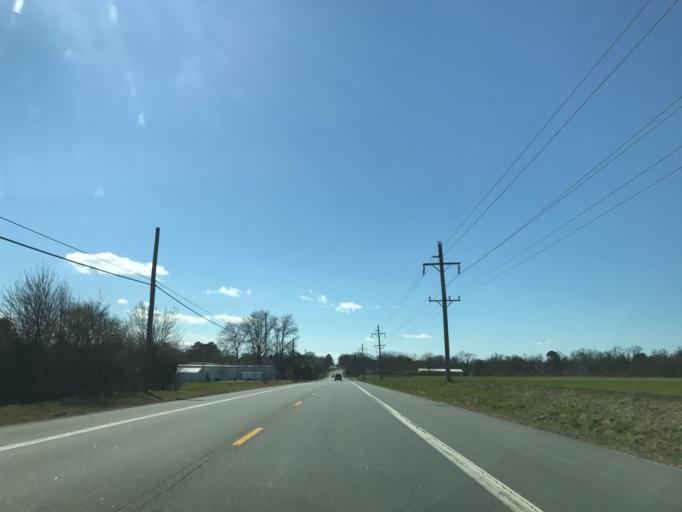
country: US
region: Maryland
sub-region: Kent County
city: Chestertown
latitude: 39.2276
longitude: -76.0548
